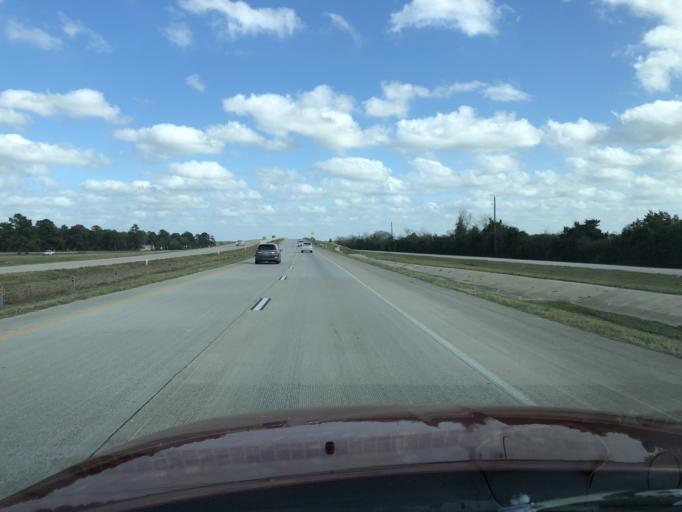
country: US
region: Texas
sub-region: Harris County
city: Cypress
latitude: 30.0498
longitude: -95.6846
